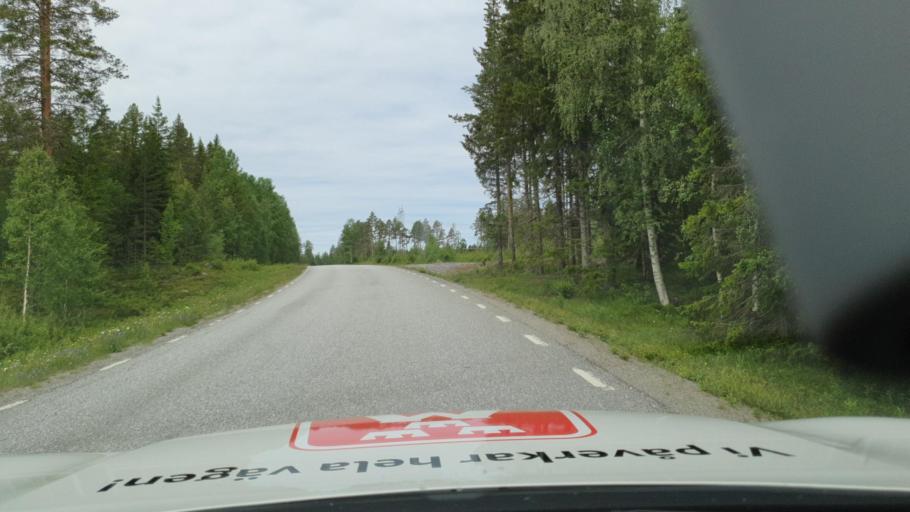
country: SE
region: Vaesterbotten
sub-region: Skelleftea Kommun
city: Langsele
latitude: 64.5328
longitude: 20.3095
